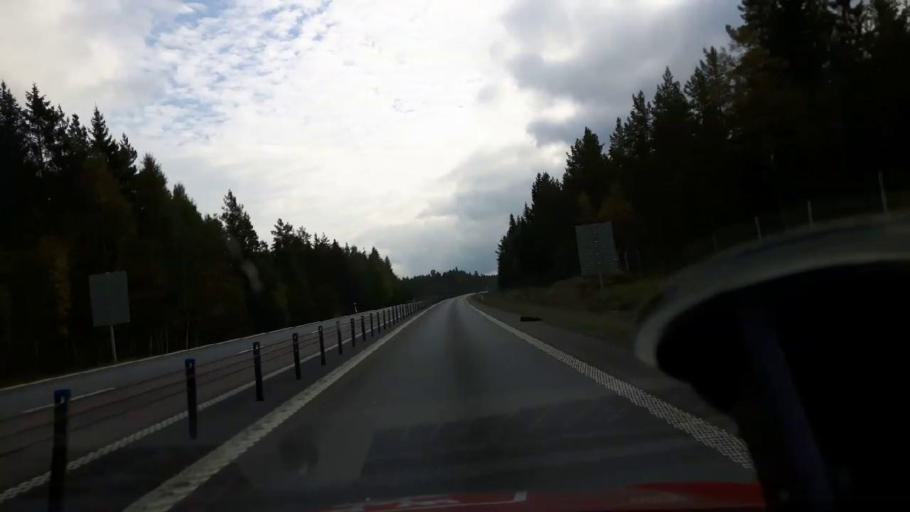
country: SE
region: Gaevleborg
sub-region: Gavle Kommun
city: Norrsundet
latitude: 60.8893
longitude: 17.0383
